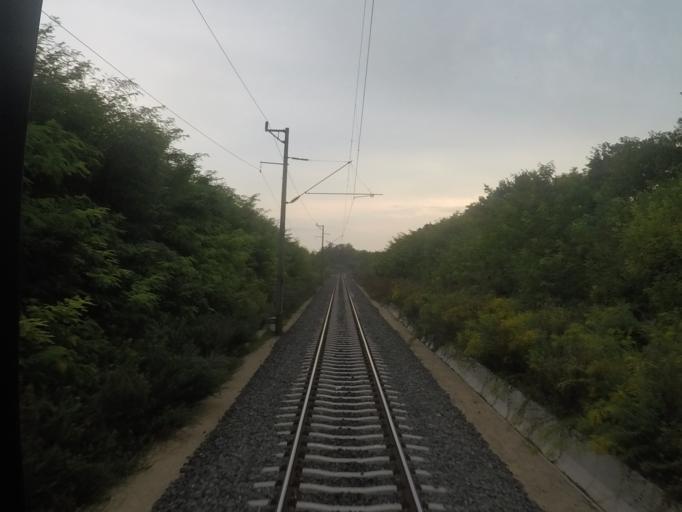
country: HU
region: Fejer
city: Lepseny
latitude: 46.9770
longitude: 18.2340
